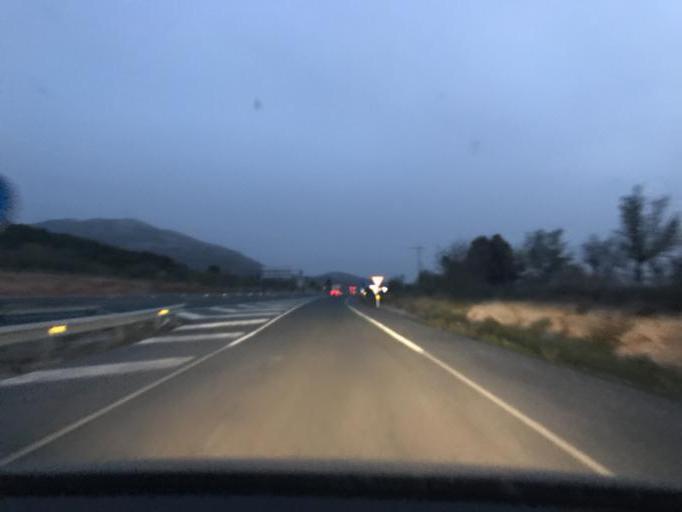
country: ES
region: Andalusia
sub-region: Provincia de Granada
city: Gor
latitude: 37.4203
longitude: -2.9174
